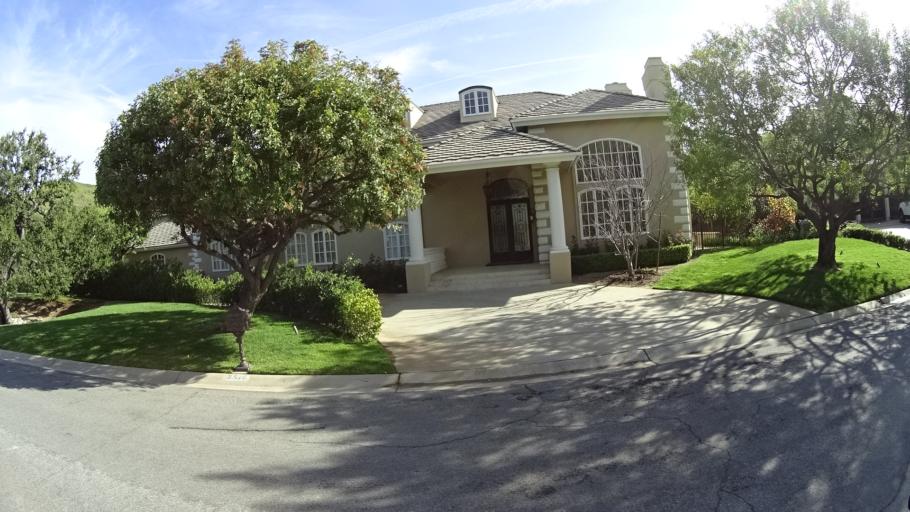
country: US
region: California
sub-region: Ventura County
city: Oak Park
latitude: 34.1922
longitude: -118.7924
